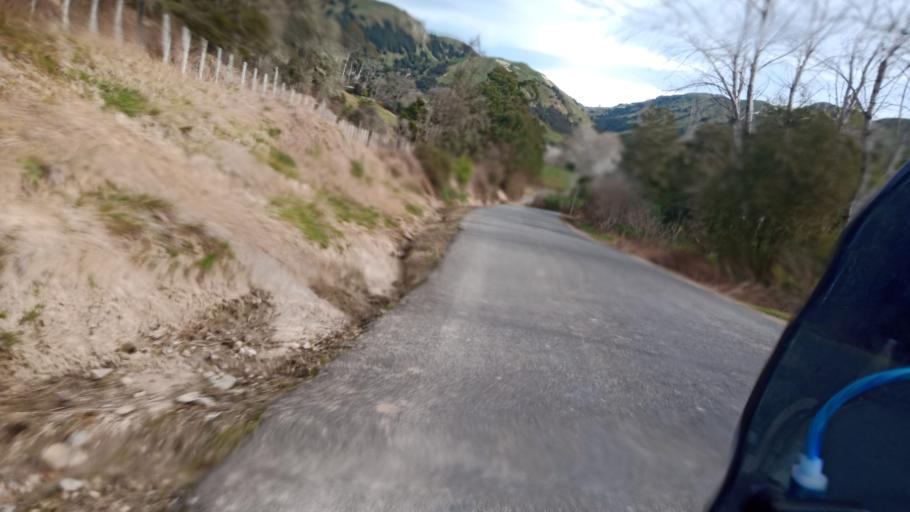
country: NZ
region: Hawke's Bay
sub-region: Wairoa District
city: Wairoa
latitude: -38.7991
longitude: 177.4595
